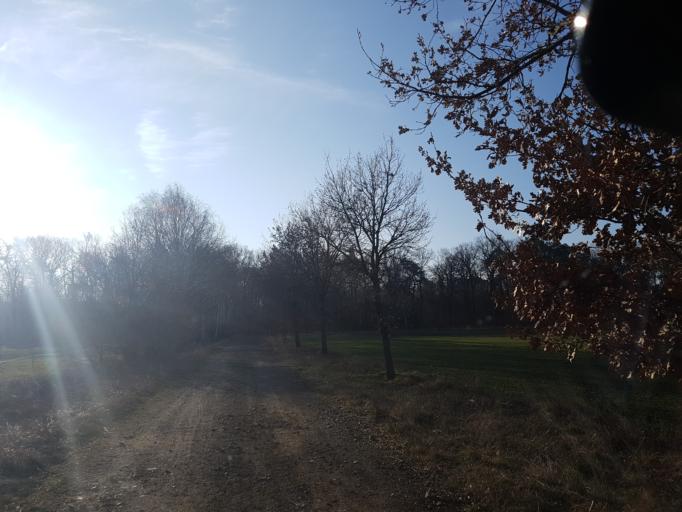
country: DE
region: Brandenburg
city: Schilda
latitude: 51.5987
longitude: 13.3334
